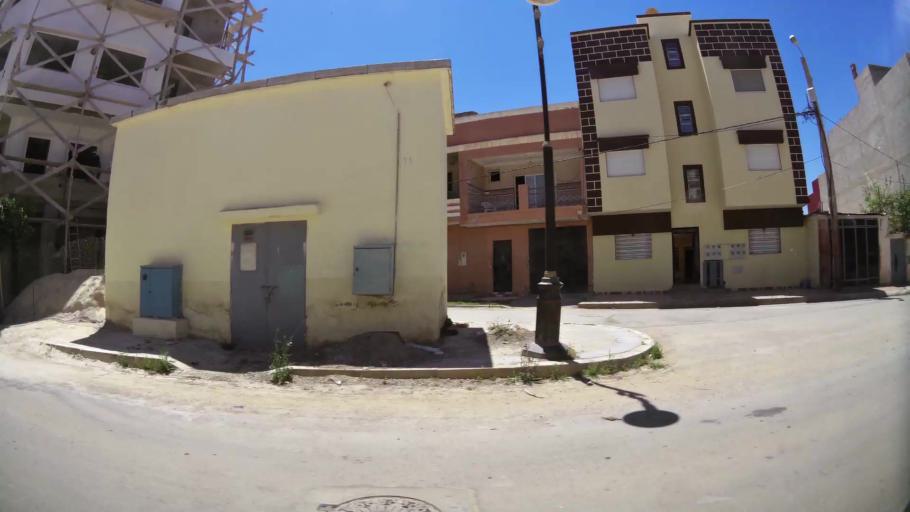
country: MA
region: Oriental
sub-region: Berkane-Taourirt
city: Madagh
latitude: 35.0817
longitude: -2.2282
